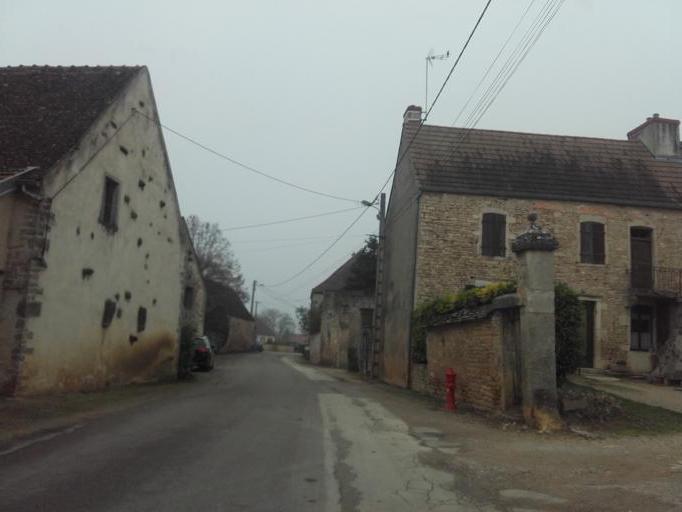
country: FR
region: Bourgogne
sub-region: Departement de la Cote-d'Or
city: Meursault
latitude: 46.9532
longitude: 4.7924
